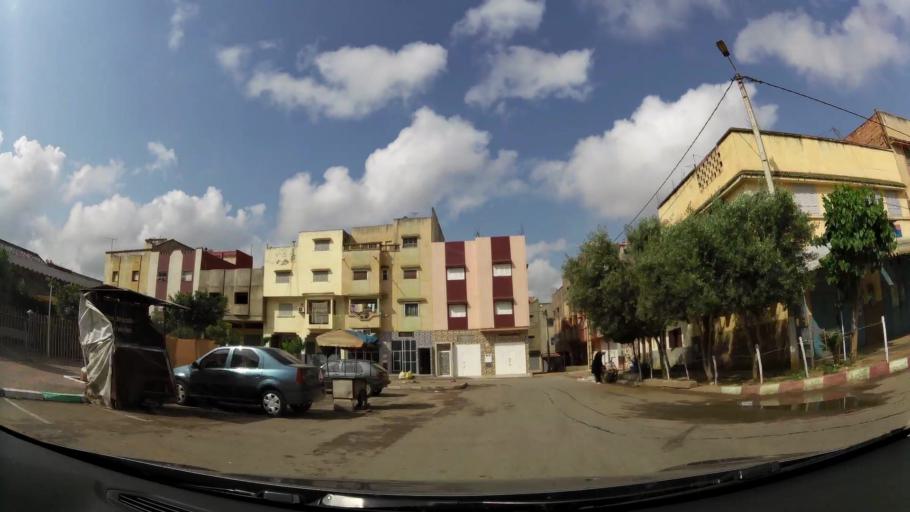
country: MA
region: Rabat-Sale-Zemmour-Zaer
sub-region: Khemisset
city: Tiflet
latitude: 33.8990
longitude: -6.3188
